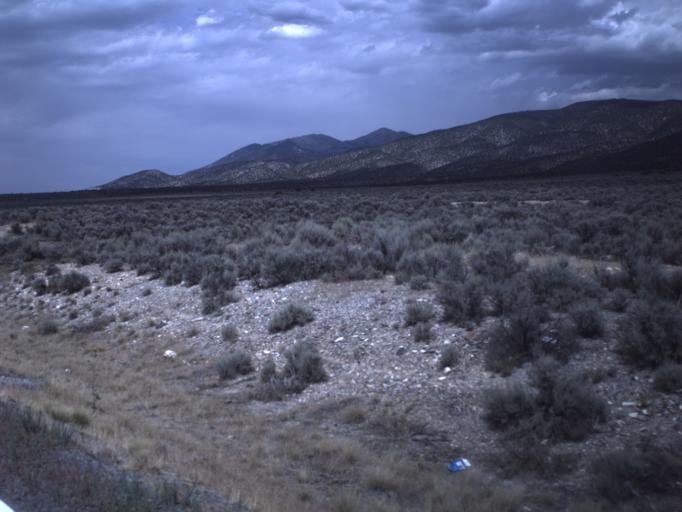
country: US
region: Utah
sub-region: Utah County
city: Eagle Mountain
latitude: 40.2760
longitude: -112.2515
